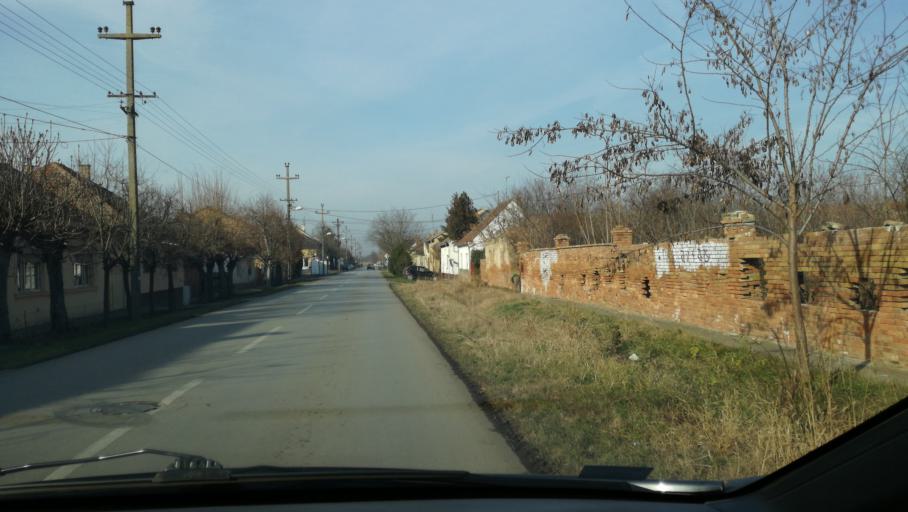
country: RS
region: Autonomna Pokrajina Vojvodina
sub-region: Severnobanatski Okrug
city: Kikinda
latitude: 45.8389
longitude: 20.4738
